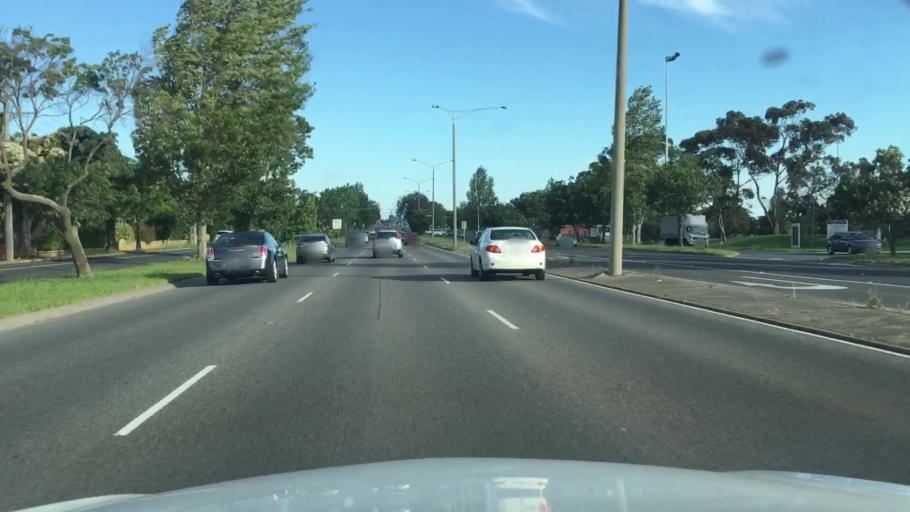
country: AU
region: Victoria
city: Clayton
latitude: -37.9071
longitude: 145.1158
